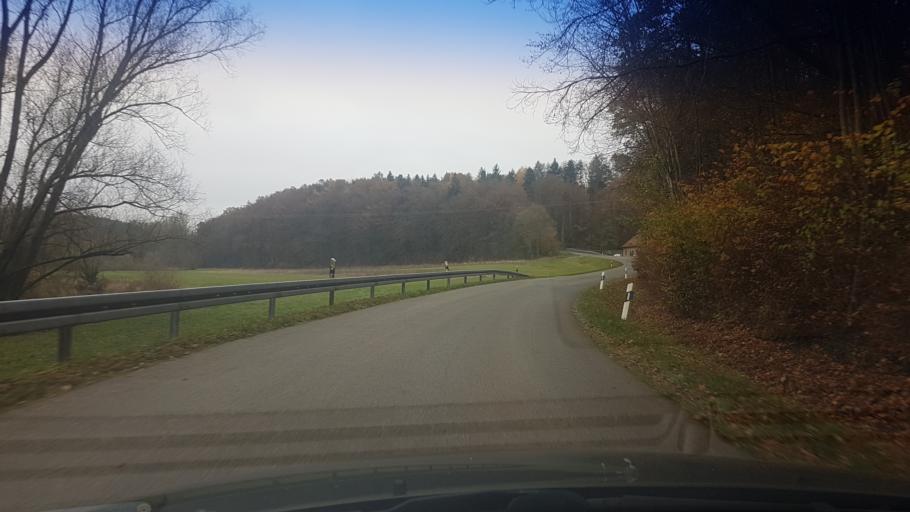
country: DE
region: Bavaria
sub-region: Upper Franconia
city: Rattelsdorf
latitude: 50.0427
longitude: 10.8748
